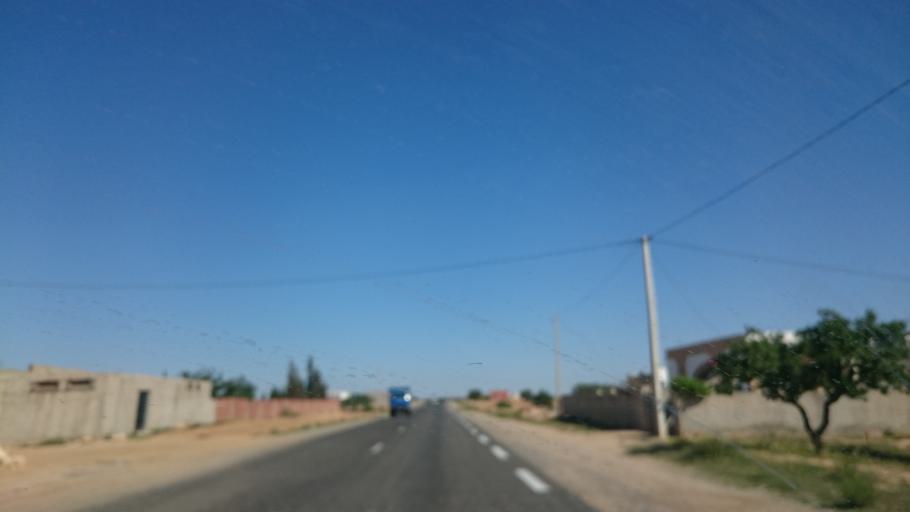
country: TN
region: Safaqis
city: Sfax
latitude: 34.7811
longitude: 10.5037
